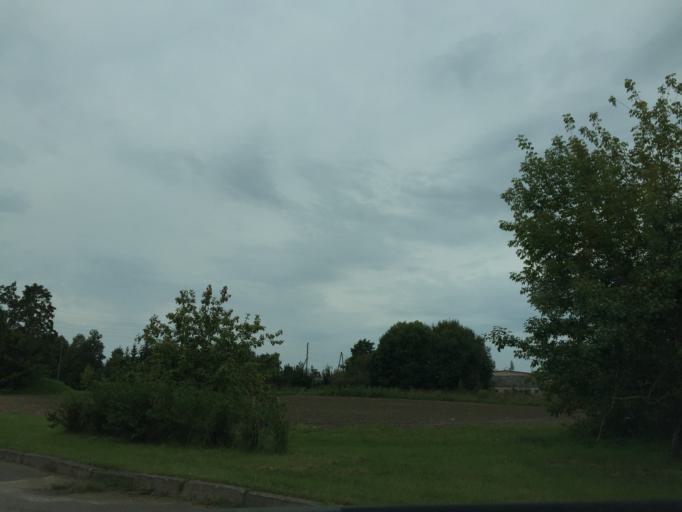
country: LV
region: Zilupes
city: Zilupe
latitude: 56.3909
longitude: 28.1384
